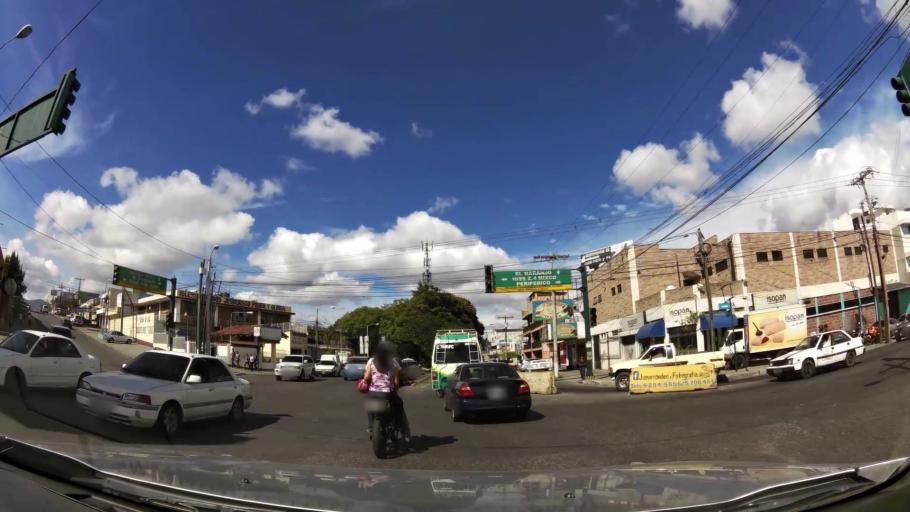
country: GT
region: Guatemala
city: Mixco
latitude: 14.6429
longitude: -90.5674
